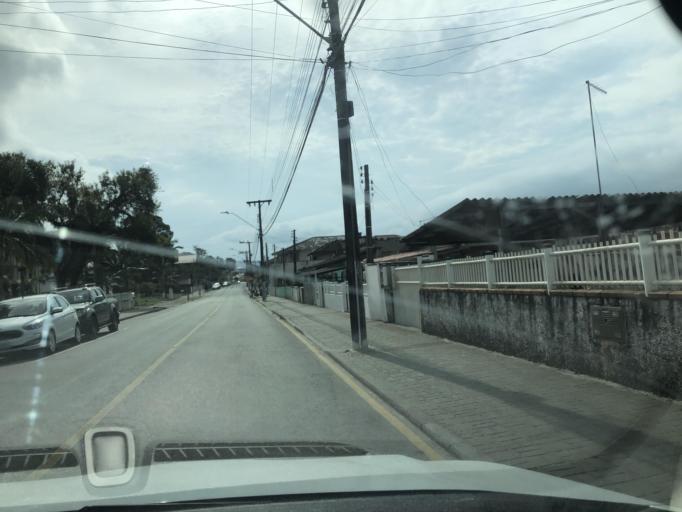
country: BR
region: Santa Catarina
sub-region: Sao Francisco Do Sul
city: Sao Francisco do Sul
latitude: -26.2302
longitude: -48.6135
